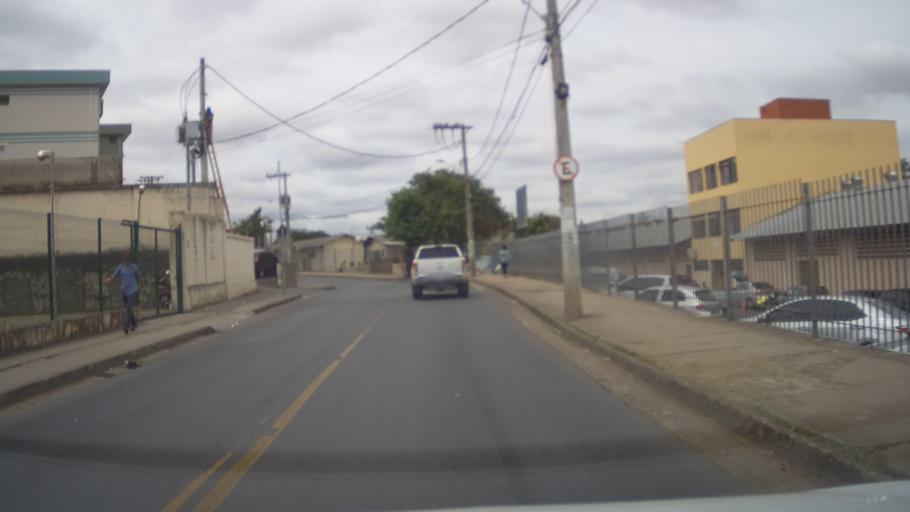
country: BR
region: Minas Gerais
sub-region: Belo Horizonte
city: Belo Horizonte
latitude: -19.8659
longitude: -43.9257
